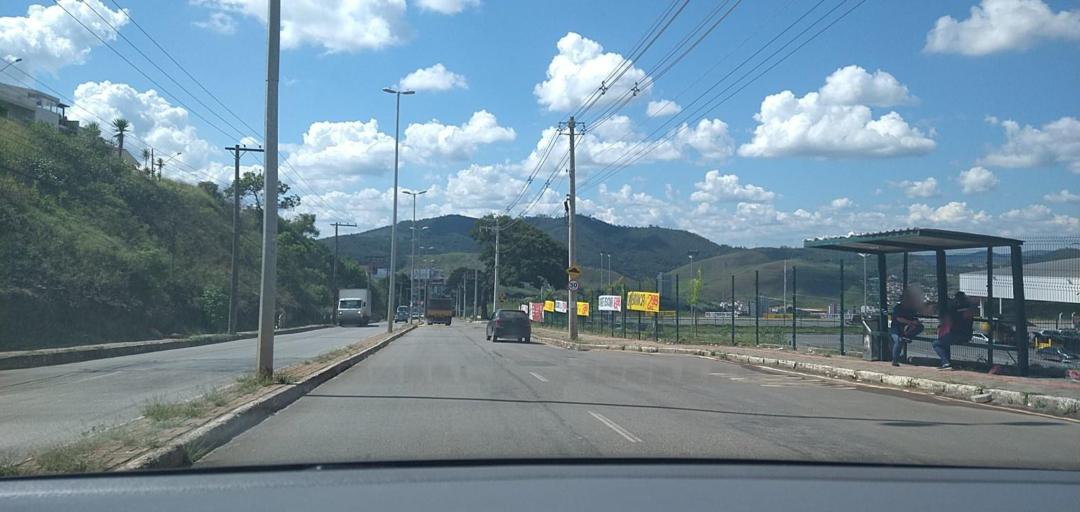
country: BR
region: Minas Gerais
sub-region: Joao Monlevade
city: Joao Monlevade
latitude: -19.8267
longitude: -43.1891
